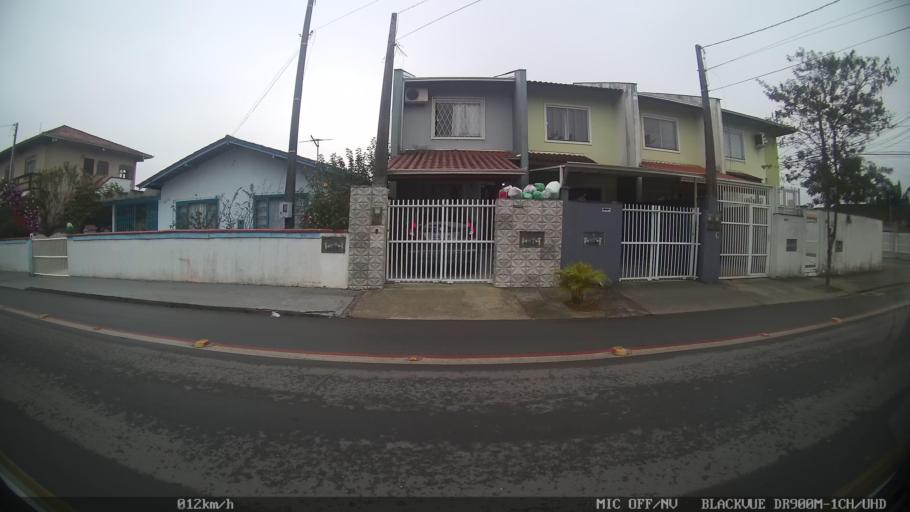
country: BR
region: Santa Catarina
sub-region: Joinville
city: Joinville
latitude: -26.2526
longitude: -48.8049
